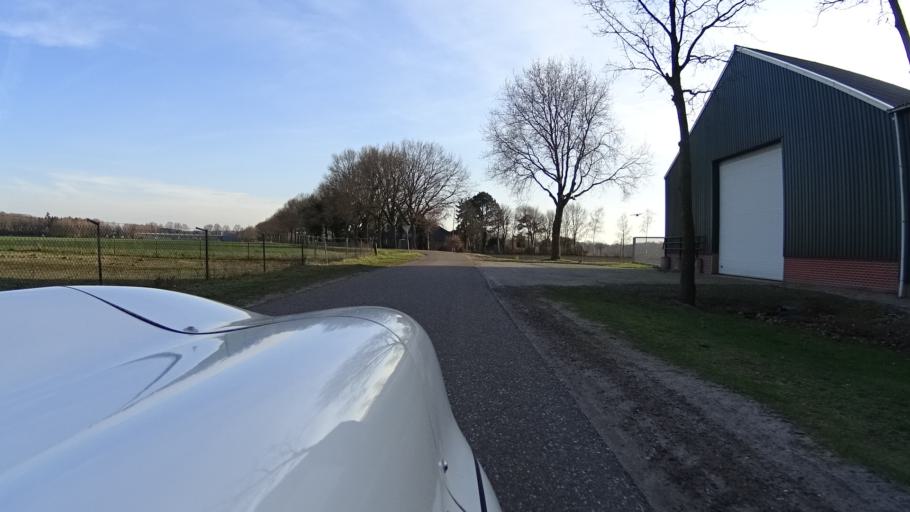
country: NL
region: North Brabant
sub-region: Gemeente Boekel
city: Boekel
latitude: 51.6029
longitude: 5.7113
